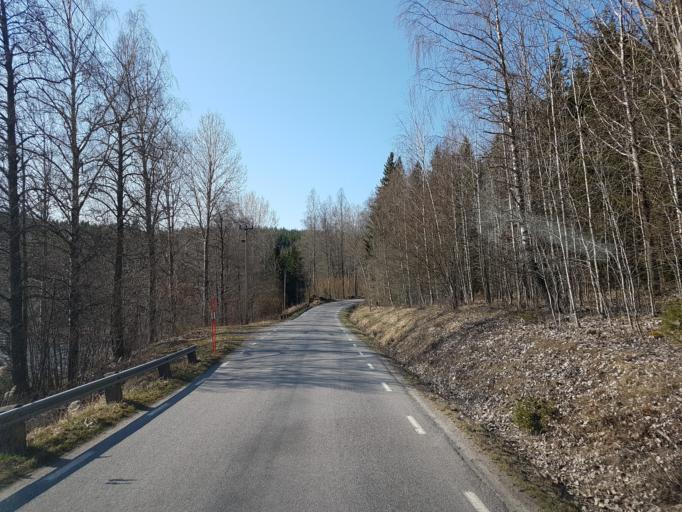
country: SE
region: Kalmar
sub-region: Vasterviks Kommun
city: Overum
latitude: 58.1743
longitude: 16.2762
